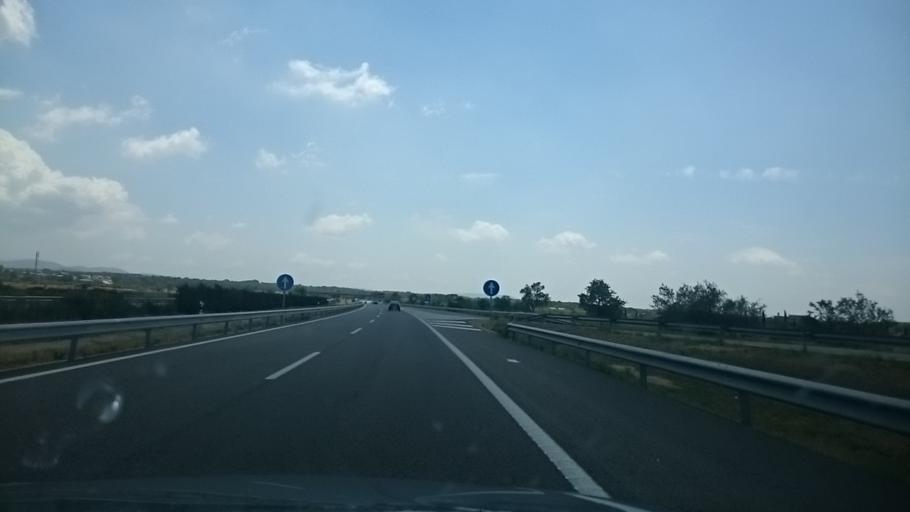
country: ES
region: Catalonia
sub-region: Provincia de Tarragona
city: El Pla de Santa Maria
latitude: 41.3529
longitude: 1.3136
